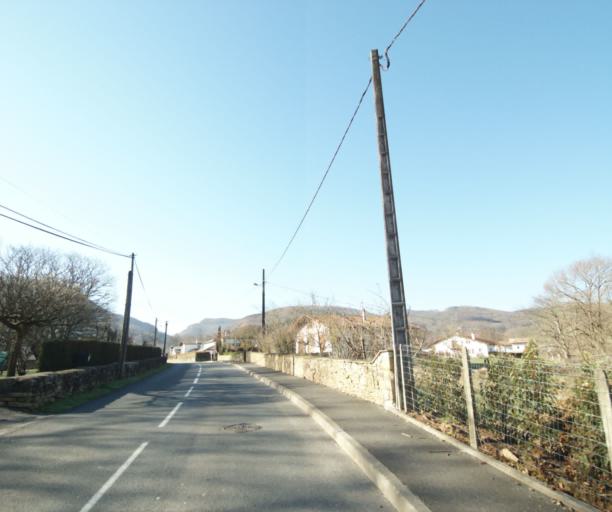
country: FR
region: Aquitaine
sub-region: Departement des Pyrenees-Atlantiques
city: Urrugne
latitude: 43.3376
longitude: -1.6682
